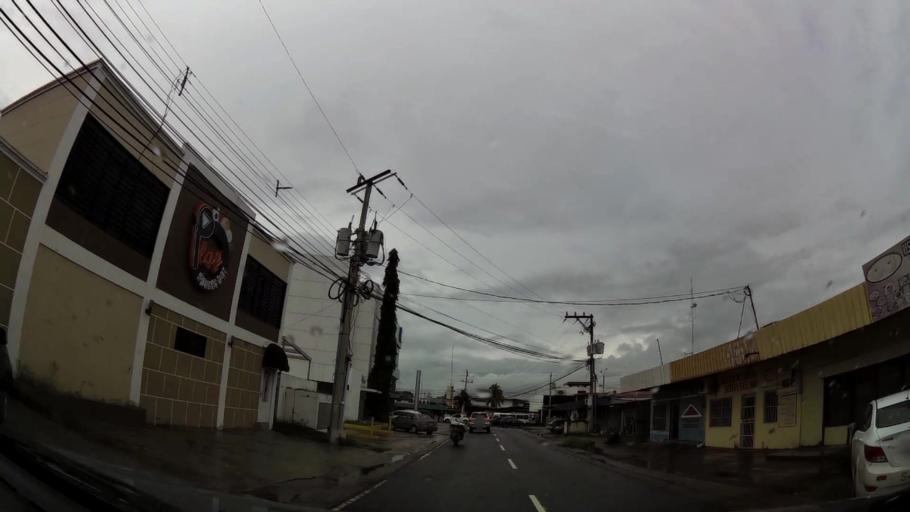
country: PA
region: Veraguas
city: Santiago de Veraguas
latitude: 8.0969
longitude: -80.9766
